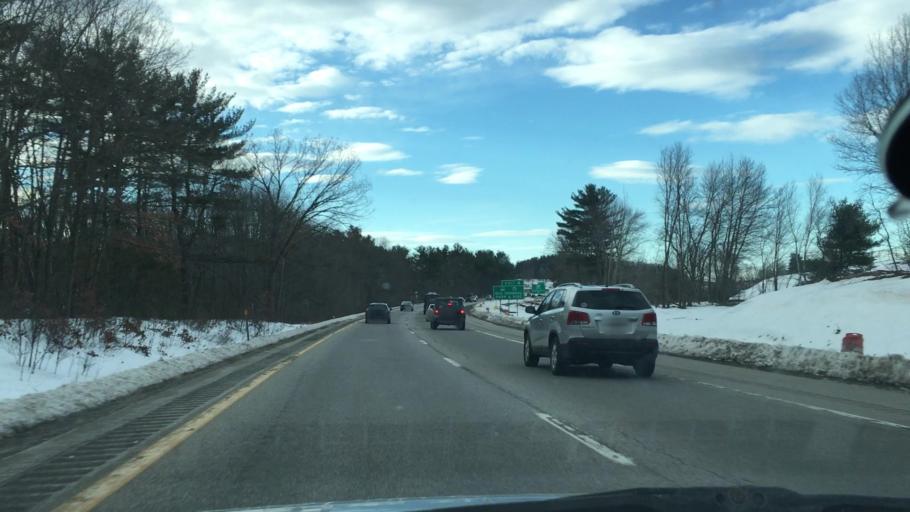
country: US
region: New Hampshire
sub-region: Rockingham County
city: Derry
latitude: 42.8624
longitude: -71.3355
